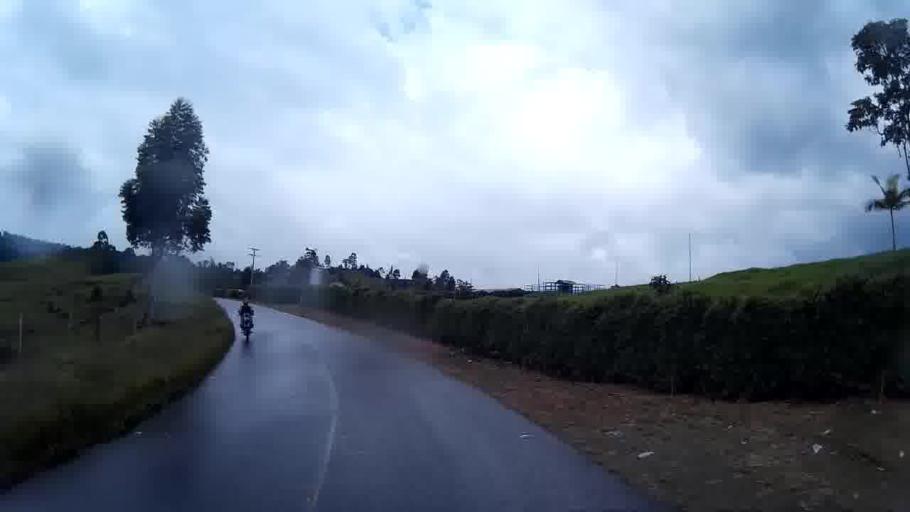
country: CO
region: Quindio
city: Filandia
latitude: 4.6799
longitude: -75.6405
